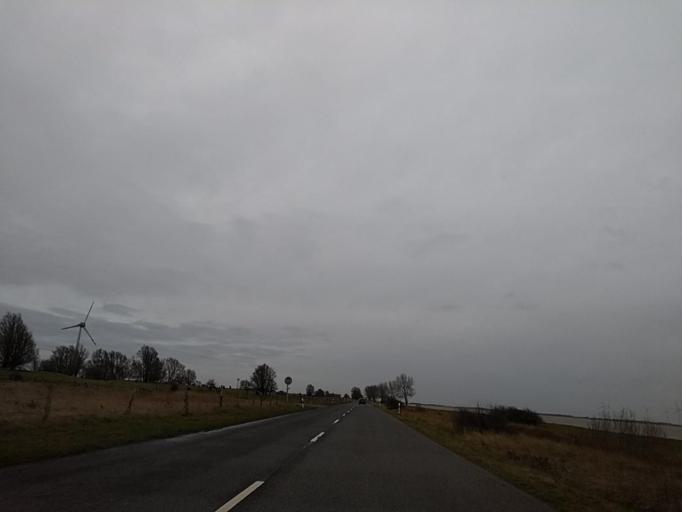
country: NL
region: Groningen
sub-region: Gemeente Delfzijl
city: Delfzijl
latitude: 53.3539
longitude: 7.0059
